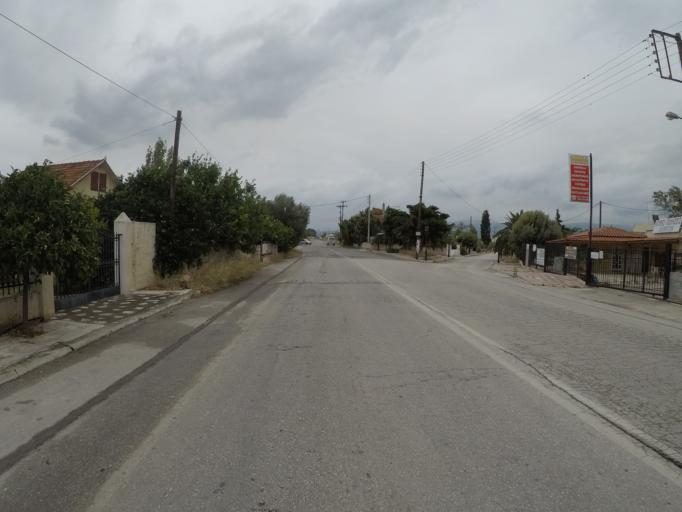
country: GR
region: Peloponnese
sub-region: Nomos Korinthias
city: Isthmia
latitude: 37.9249
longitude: 23.0196
